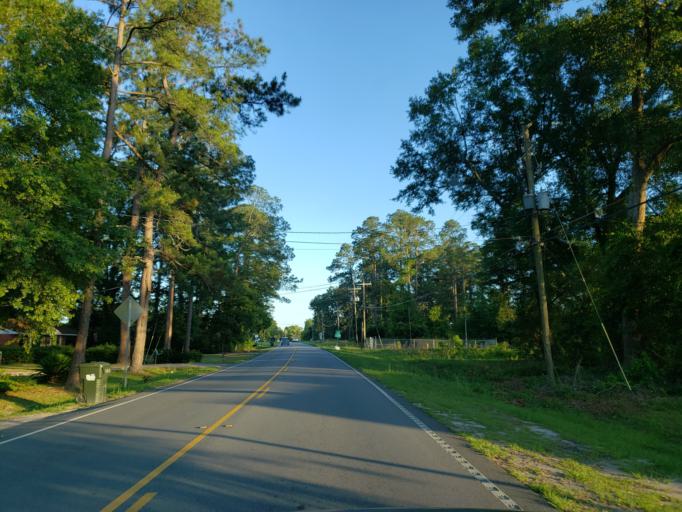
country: US
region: Georgia
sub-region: Lowndes County
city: Valdosta
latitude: 30.7666
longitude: -83.2667
